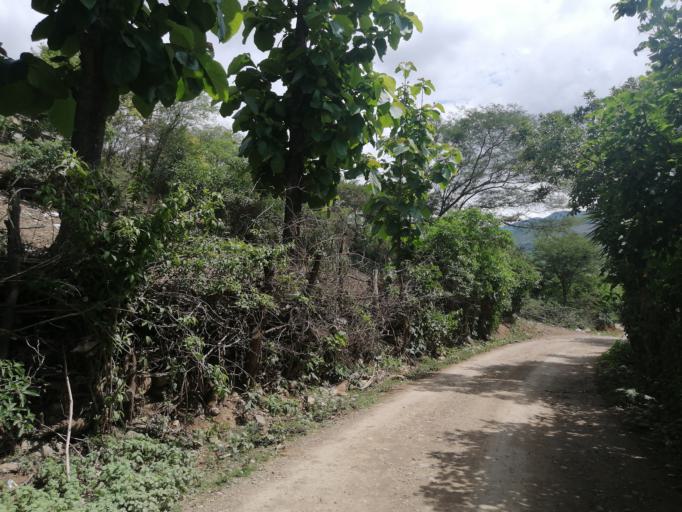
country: EC
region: Loja
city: Catacocha
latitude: -4.0155
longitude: -79.6827
